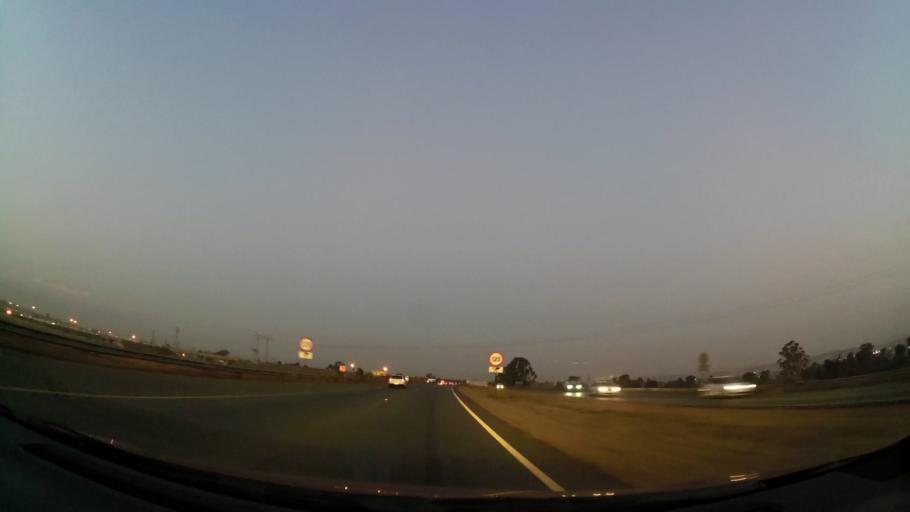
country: ZA
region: Gauteng
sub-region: City of Johannesburg Metropolitan Municipality
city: Soweto
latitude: -26.2951
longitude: 27.8416
